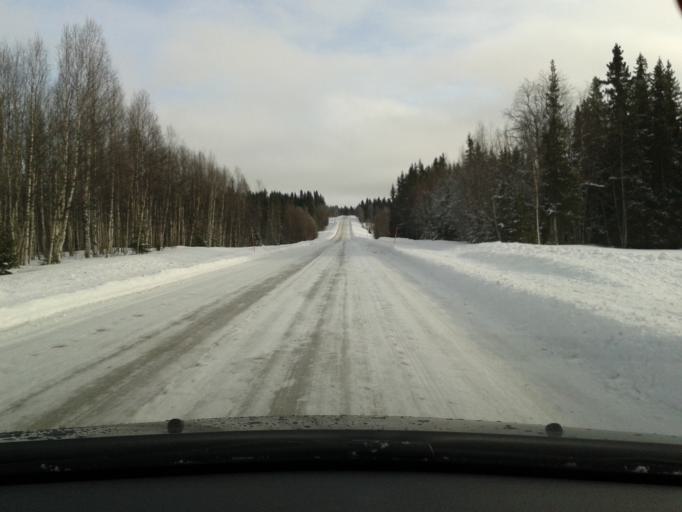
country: SE
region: Vaesterbotten
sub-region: Vilhelmina Kommun
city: Sjoberg
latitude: 64.7958
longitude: 16.0575
